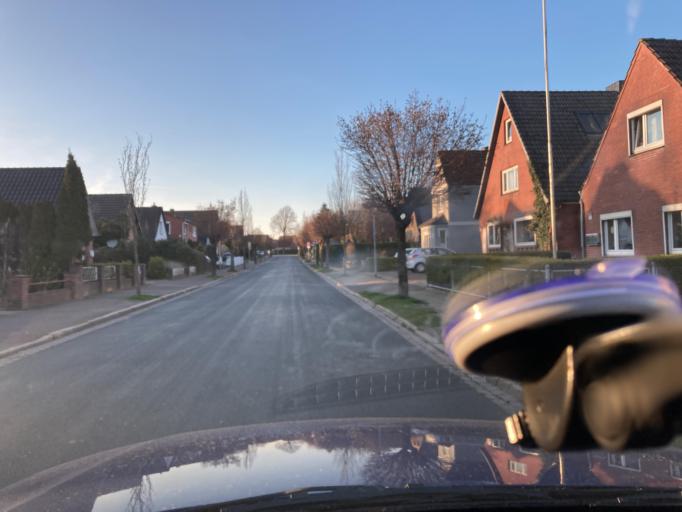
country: DE
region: Schleswig-Holstein
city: Wesseln
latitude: 54.1970
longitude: 9.0826
